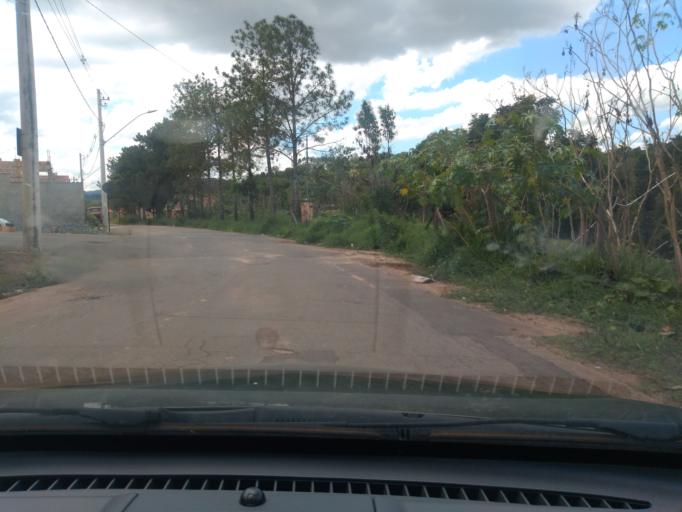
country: BR
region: Minas Gerais
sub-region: Tres Coracoes
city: Tres Coracoes
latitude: -21.6733
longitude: -45.2647
